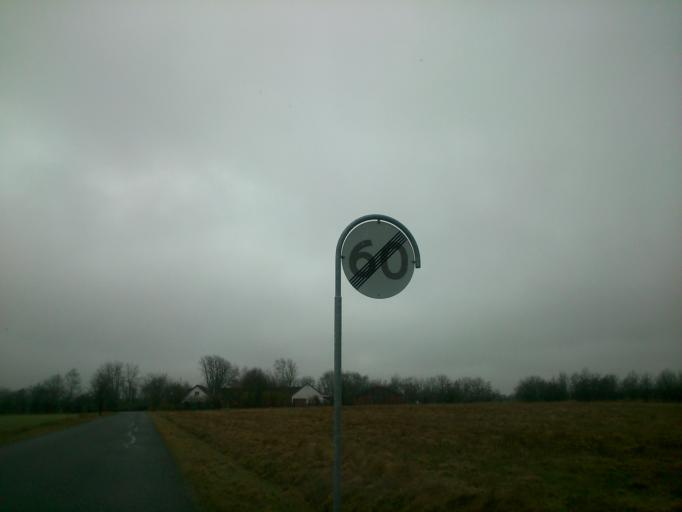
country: DK
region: Central Jutland
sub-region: Ringkobing-Skjern Kommune
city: Videbaek
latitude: 56.0497
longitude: 8.6358
